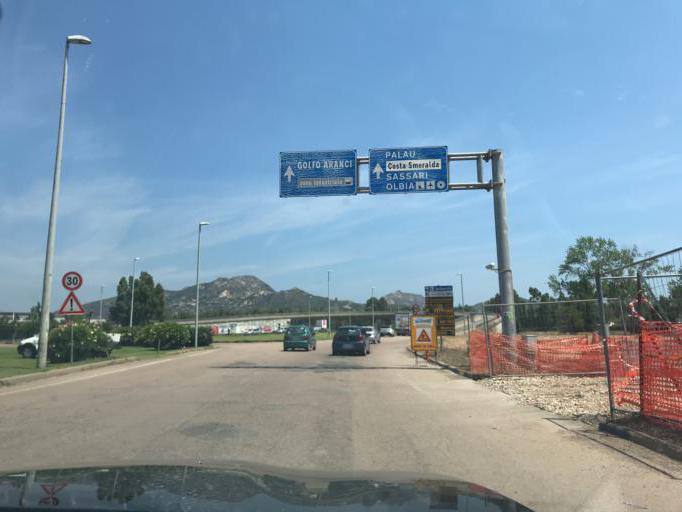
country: IT
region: Sardinia
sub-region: Provincia di Olbia-Tempio
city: Olbia
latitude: 40.9312
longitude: 9.5099
